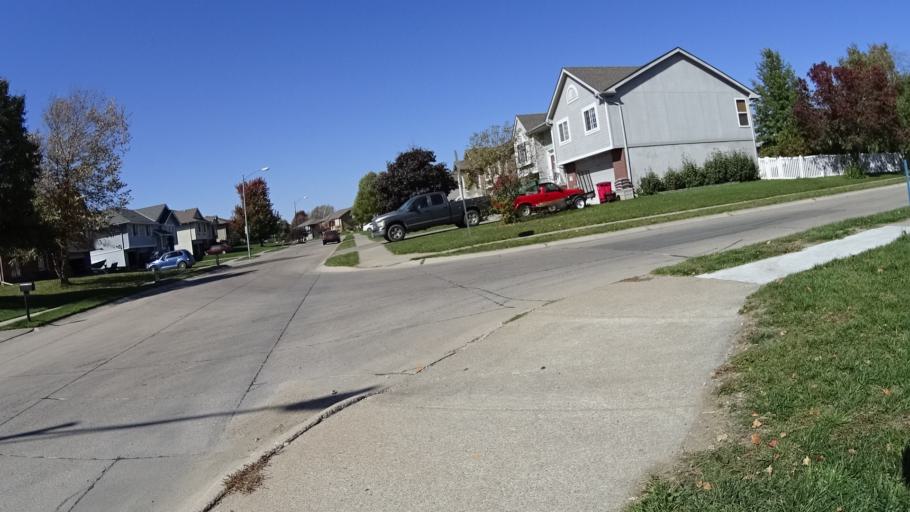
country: US
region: Nebraska
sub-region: Sarpy County
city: Papillion
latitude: 41.1541
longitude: -96.0117
